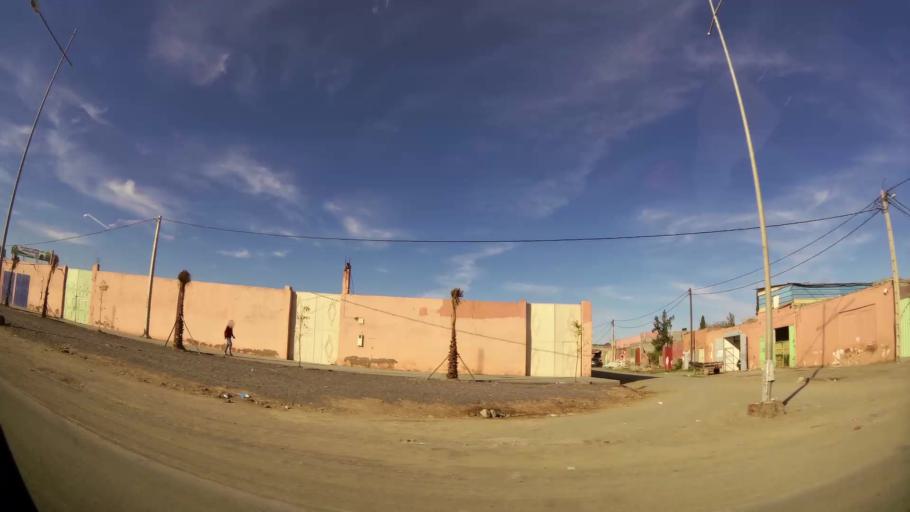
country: MA
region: Marrakech-Tensift-Al Haouz
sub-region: Marrakech
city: Marrakesh
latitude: 31.7155
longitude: -8.0764
